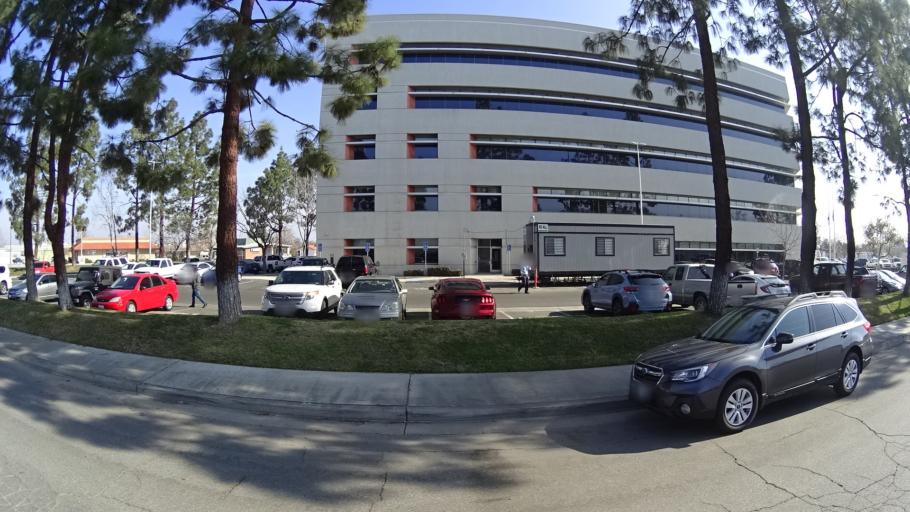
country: US
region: California
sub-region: Kern County
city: Bakersfield
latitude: 35.3839
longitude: -119.0152
